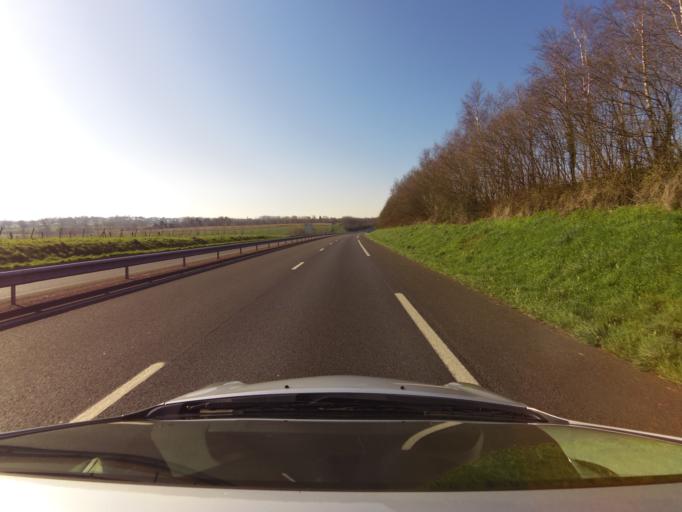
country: FR
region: Lower Normandy
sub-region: Departement de la Manche
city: Saint-James
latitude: 48.5396
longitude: -1.3410
